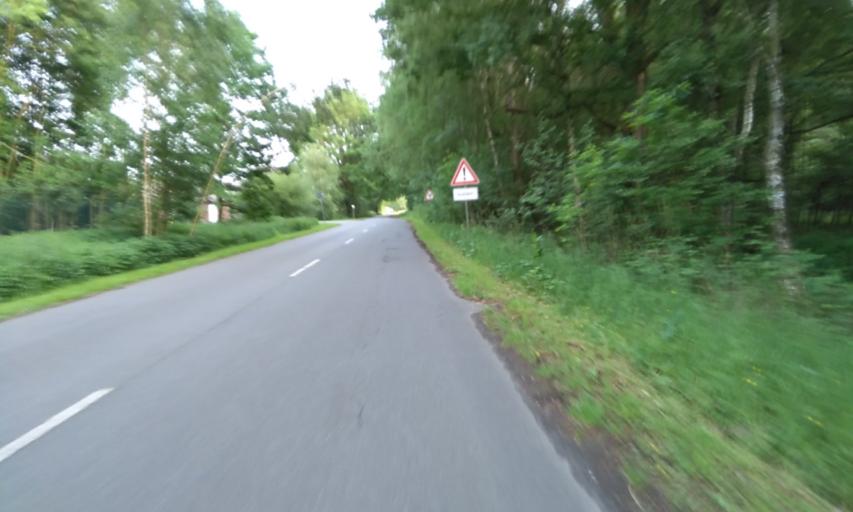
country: DE
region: Lower Saxony
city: Bargstedt
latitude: 53.4953
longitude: 9.4594
